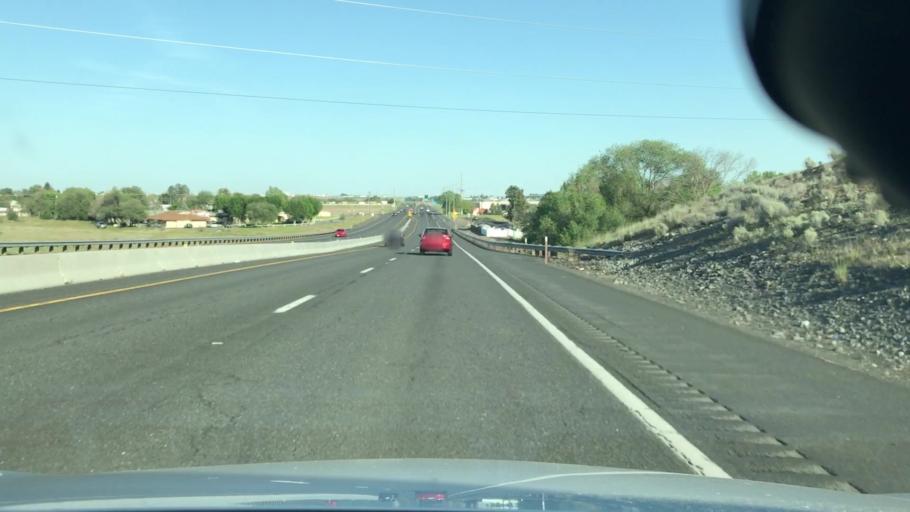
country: US
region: Washington
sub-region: Grant County
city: Moses Lake
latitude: 47.1519
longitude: -119.3001
